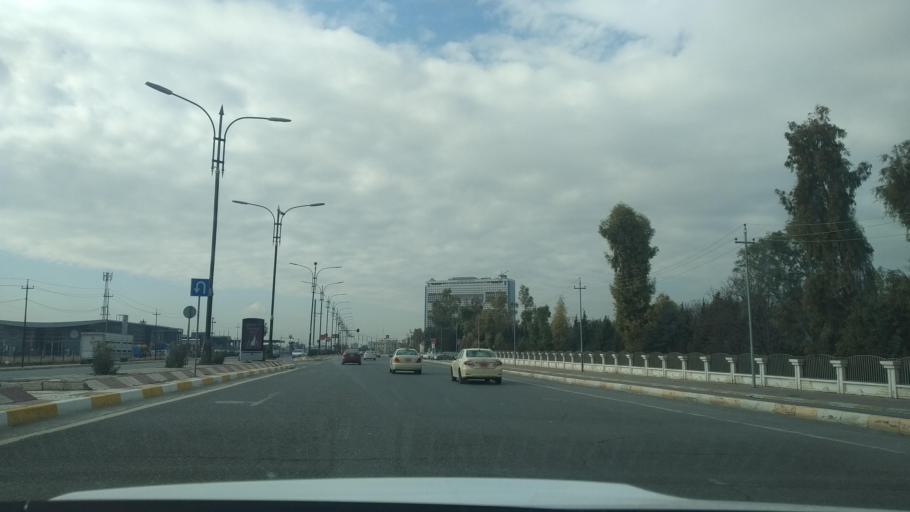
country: IQ
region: Arbil
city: Erbil
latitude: 36.1878
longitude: 43.9895
